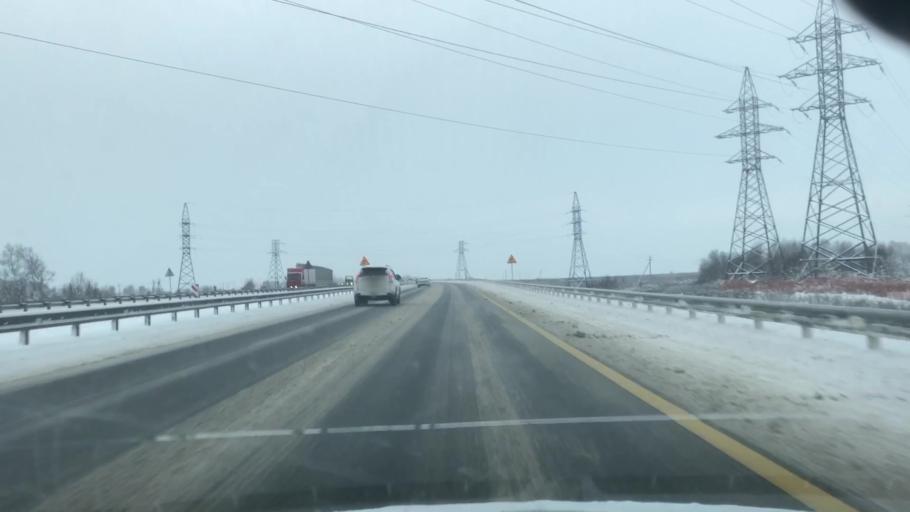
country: RU
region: Moskovskaya
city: Mikhnevo
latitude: 55.1208
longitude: 37.9301
